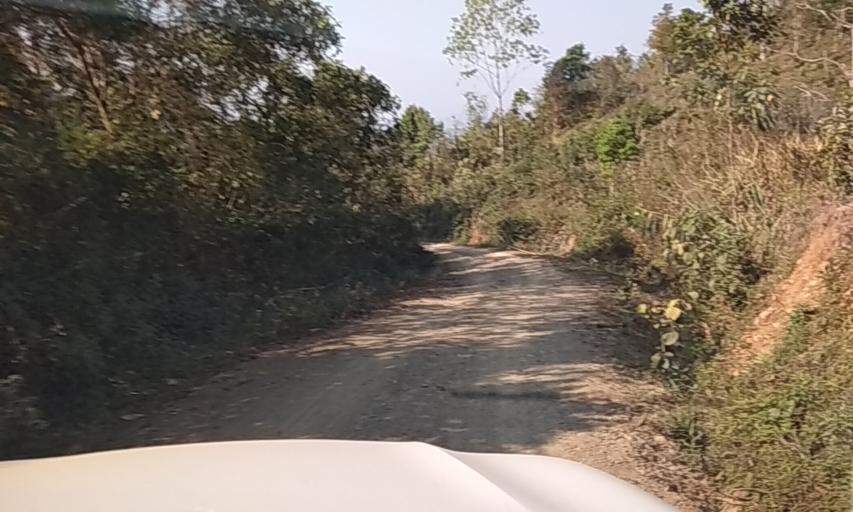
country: LA
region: Phongsali
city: Phongsali
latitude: 21.6935
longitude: 102.0905
